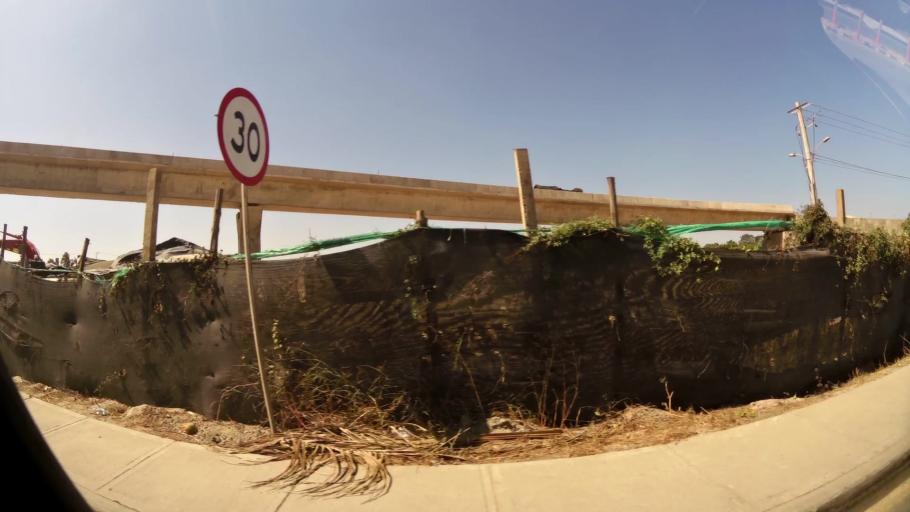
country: CO
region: Atlantico
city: Barranquilla
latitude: 10.9515
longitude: -74.7671
